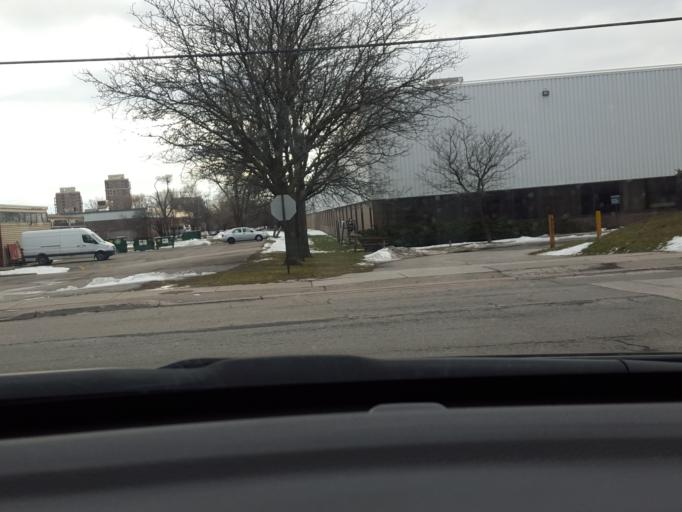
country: CA
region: Ontario
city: Willowdale
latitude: 43.7288
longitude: -79.3460
